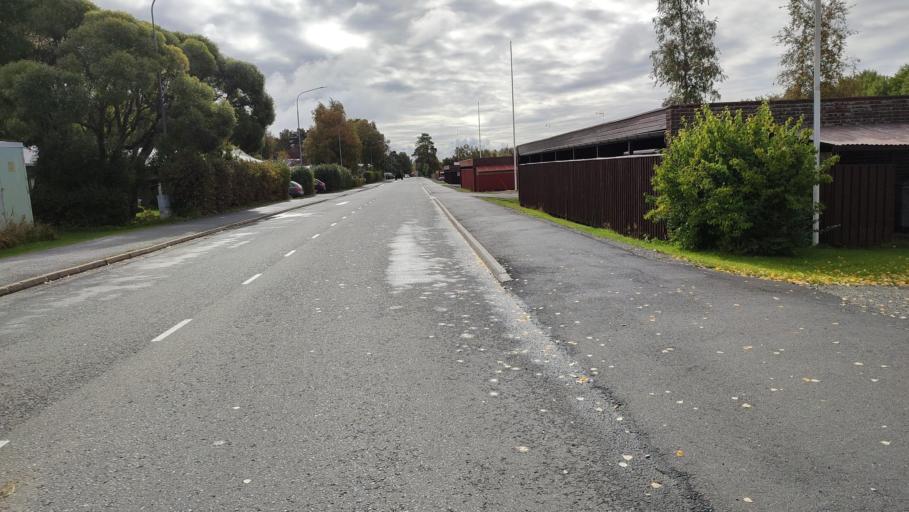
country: FI
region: Ostrobothnia
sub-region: Sydosterbotten
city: Kristinestad
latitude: 62.2733
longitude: 21.3671
